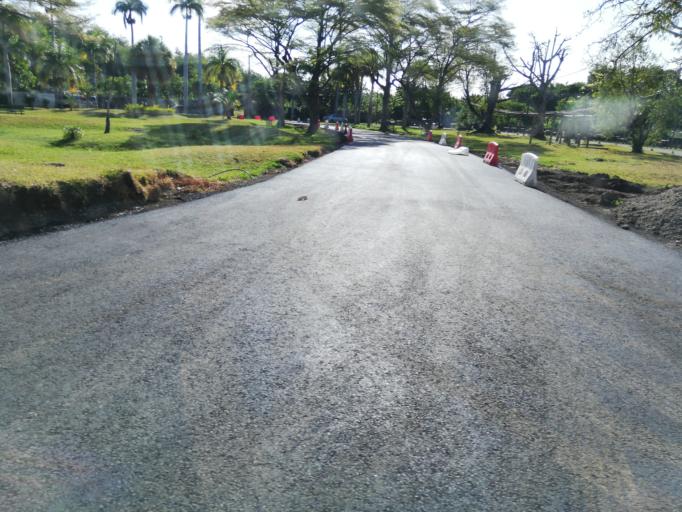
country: MU
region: Port Louis
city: Port Louis
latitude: -20.1575
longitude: 57.4872
